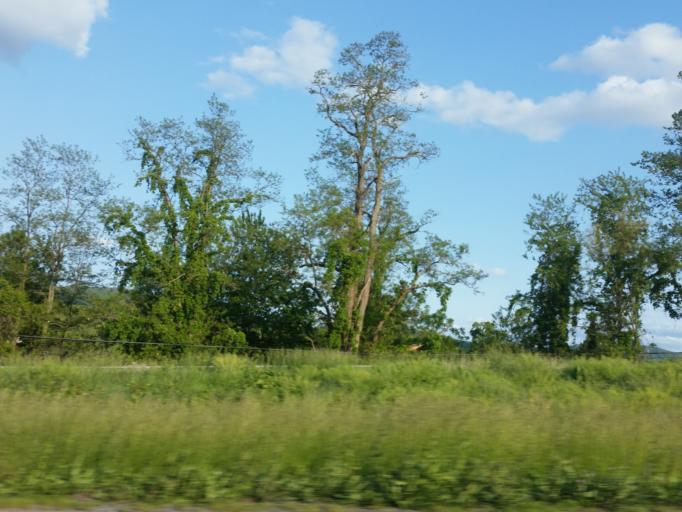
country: US
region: Virginia
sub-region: Russell County
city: Honaker
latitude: 36.9354
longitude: -81.9688
